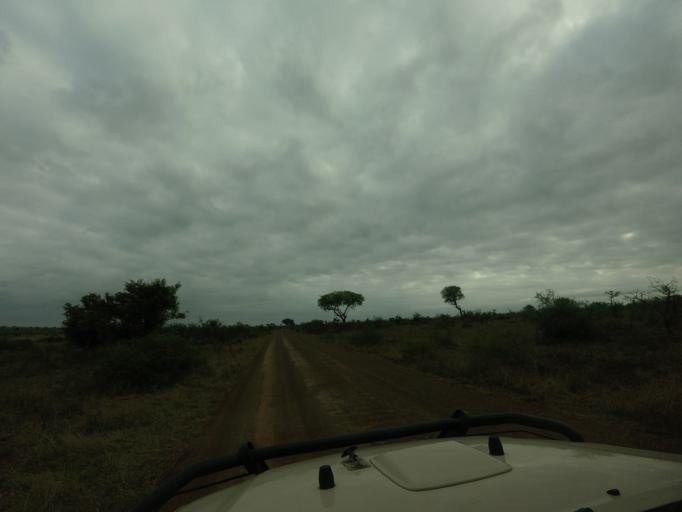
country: ZA
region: Mpumalanga
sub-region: Ehlanzeni District
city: Komatipoort
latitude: -25.3169
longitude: 31.9096
